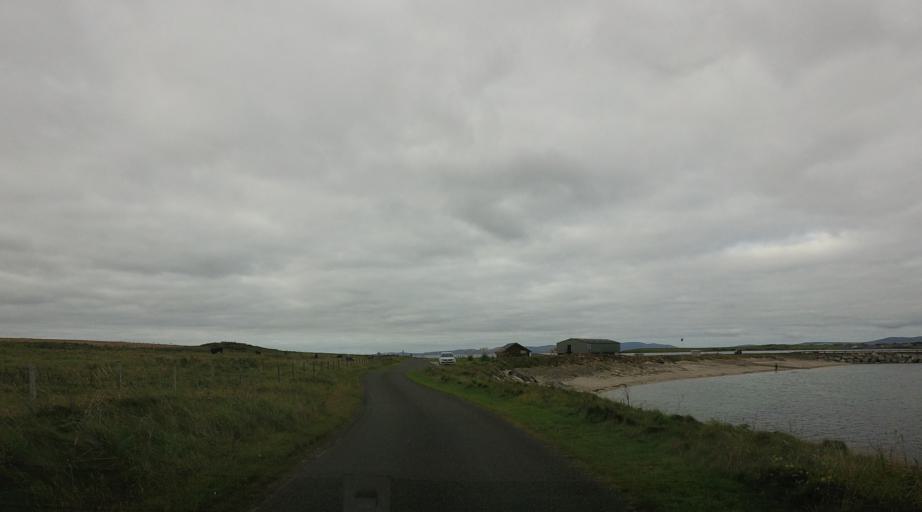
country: GB
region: Scotland
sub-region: Orkney Islands
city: Kirkwall
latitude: 58.8898
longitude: -2.8919
